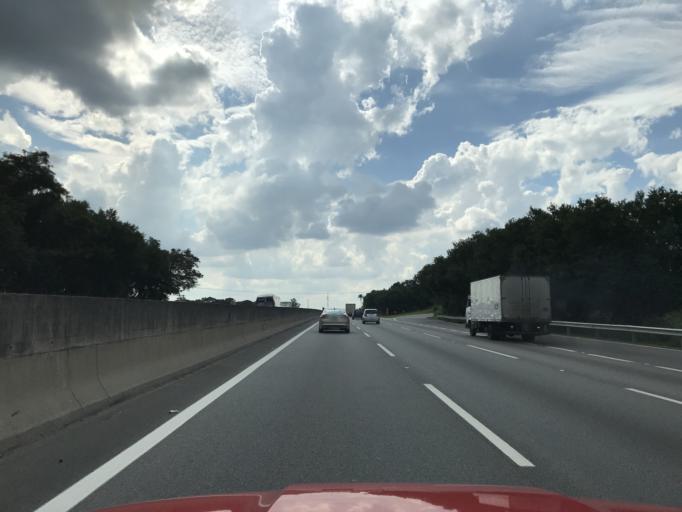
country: BR
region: Sao Paulo
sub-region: Jundiai
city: Jundiai
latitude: -23.1500
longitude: -46.9368
